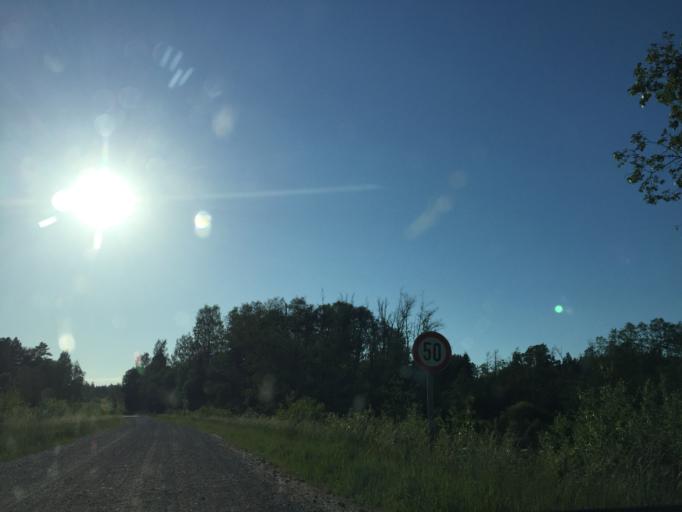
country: LV
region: Kandava
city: Kandava
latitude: 56.8583
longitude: 22.6766
